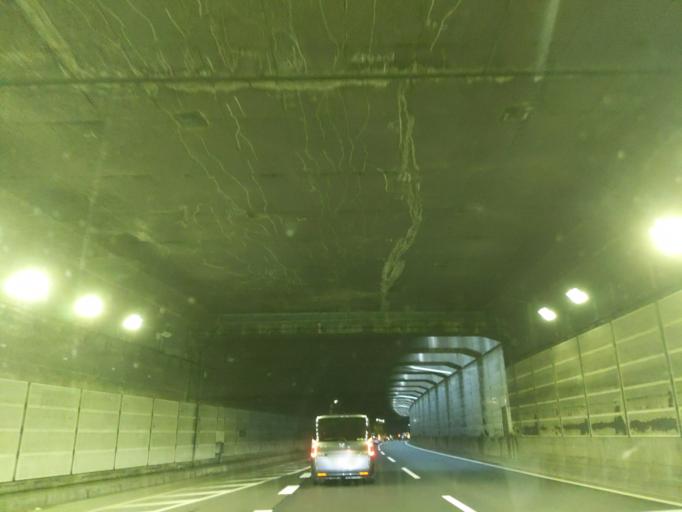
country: JP
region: Miyagi
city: Tomiya
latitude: 38.3339
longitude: 140.8866
